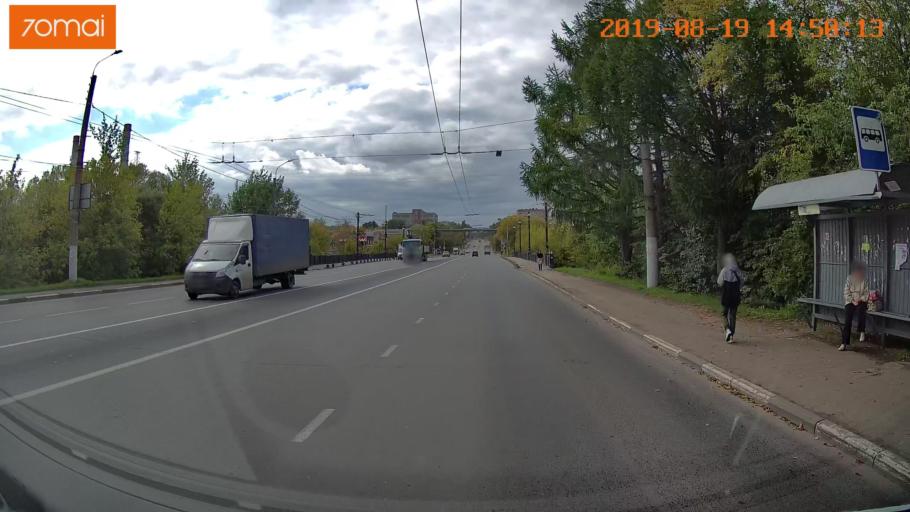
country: RU
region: Ivanovo
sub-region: Gorod Ivanovo
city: Ivanovo
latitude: 56.9938
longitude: 41.0175
